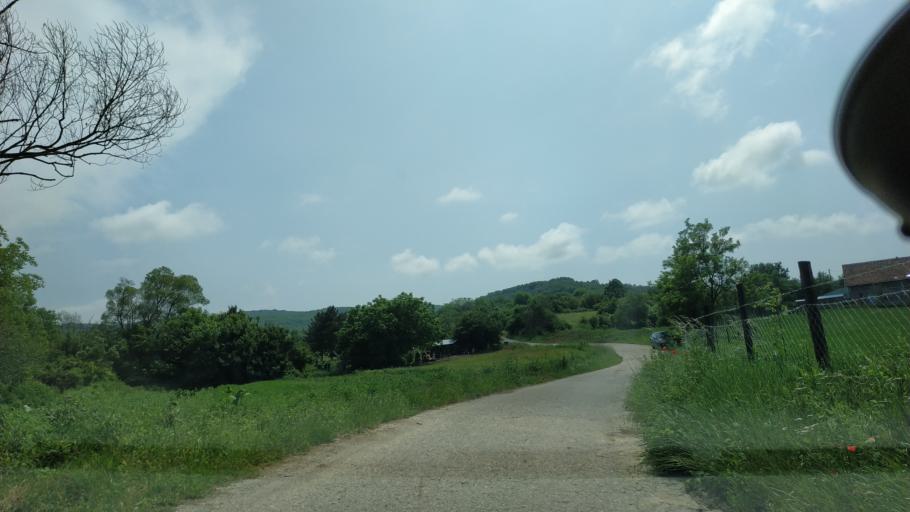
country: RS
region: Central Serbia
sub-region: Nisavski Okrug
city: Aleksinac
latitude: 43.4199
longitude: 21.7175
